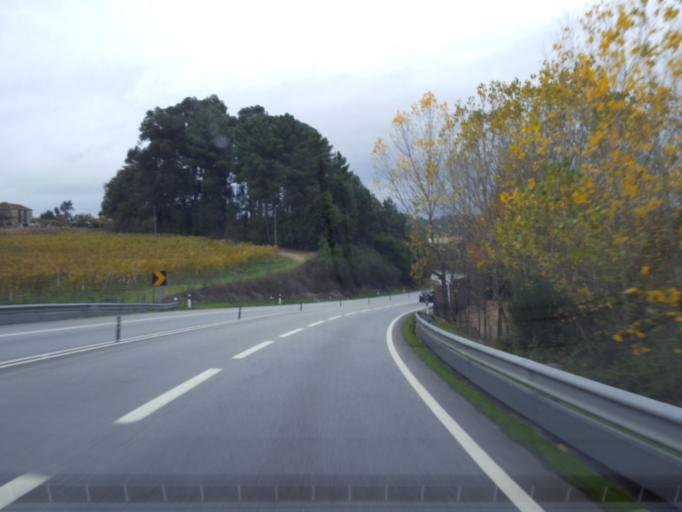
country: PT
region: Porto
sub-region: Lousada
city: Meinedo
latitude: 41.2304
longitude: -8.2003
